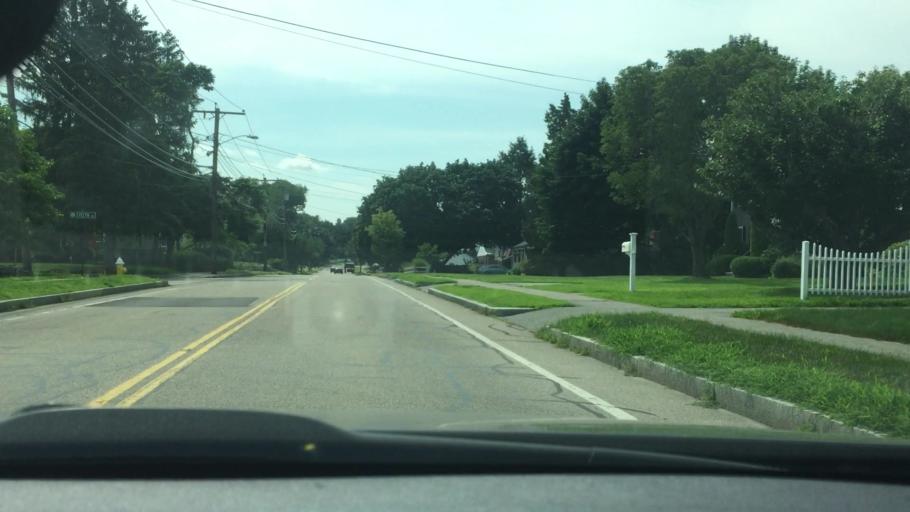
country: US
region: Massachusetts
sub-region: Norfolk County
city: Needham
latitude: 42.3035
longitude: -71.2353
